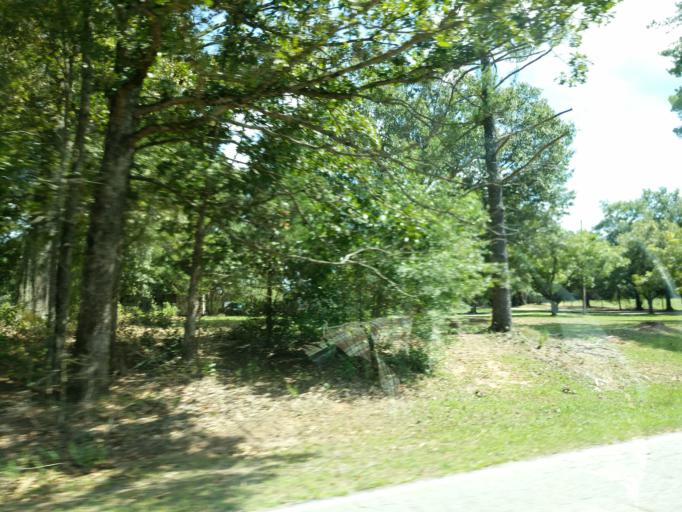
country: US
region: South Carolina
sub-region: Spartanburg County
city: Woodruff
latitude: 34.7122
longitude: -82.0469
